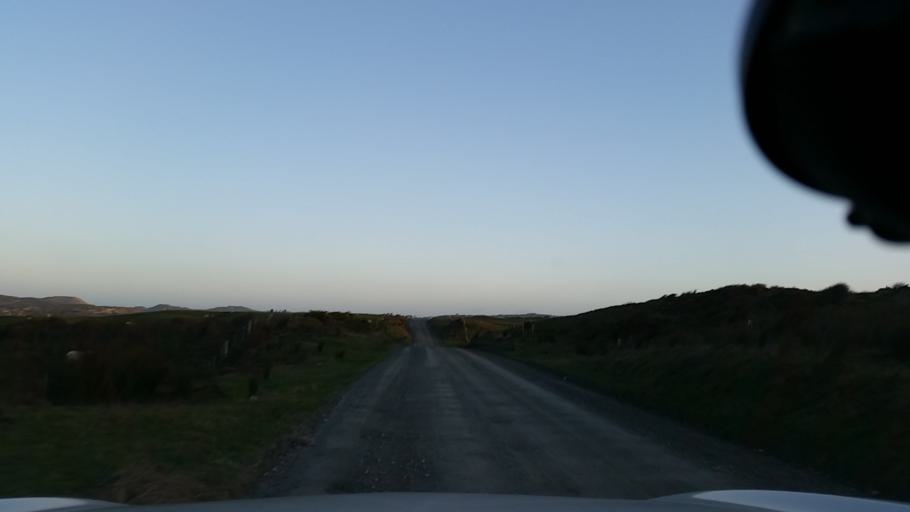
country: NZ
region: Chatham Islands
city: Waitangi
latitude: -43.8265
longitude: -176.5632
